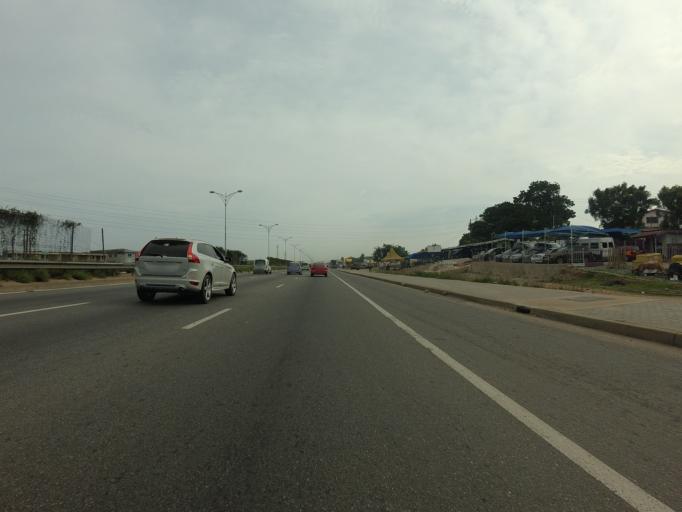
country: GH
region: Greater Accra
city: Gbawe
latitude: 5.5783
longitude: -0.2789
